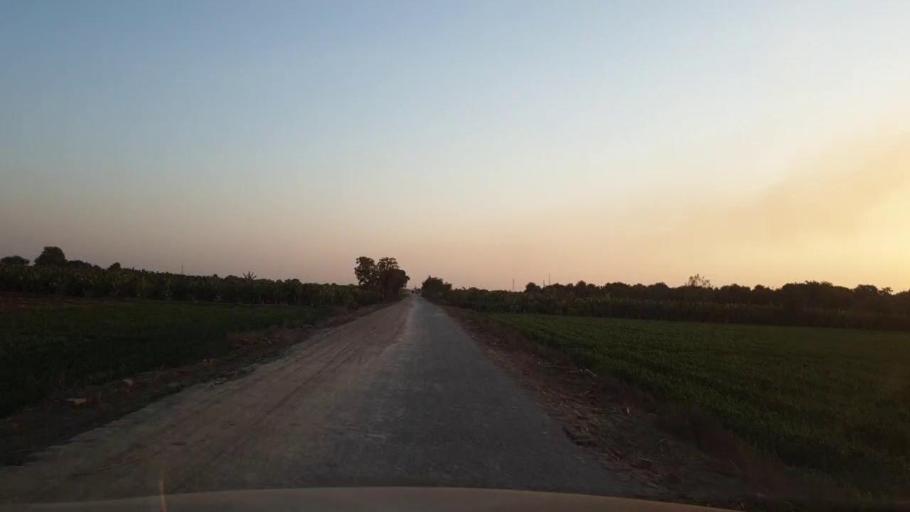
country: PK
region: Sindh
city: Tando Allahyar
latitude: 25.5319
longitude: 68.6262
